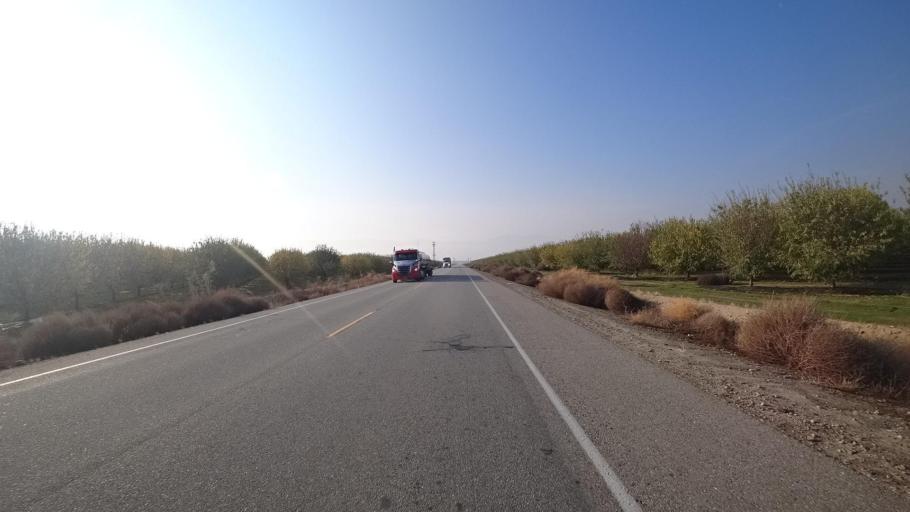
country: US
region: California
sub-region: Kern County
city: Lebec
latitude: 35.0221
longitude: -118.9323
